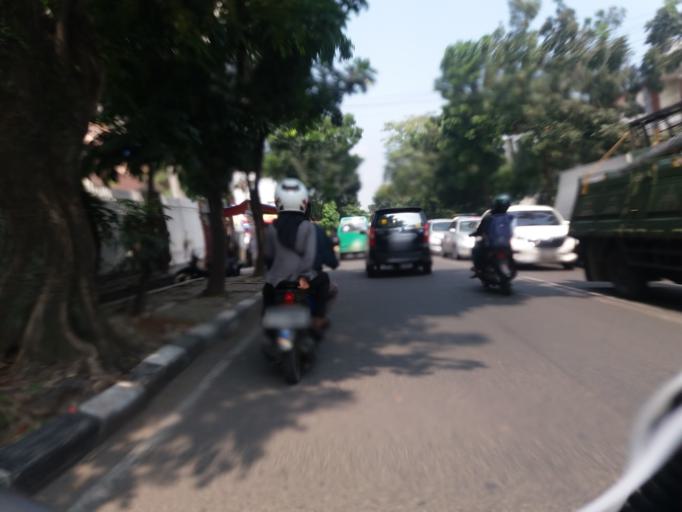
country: ID
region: West Java
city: Bandung
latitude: -6.9120
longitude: 107.5780
